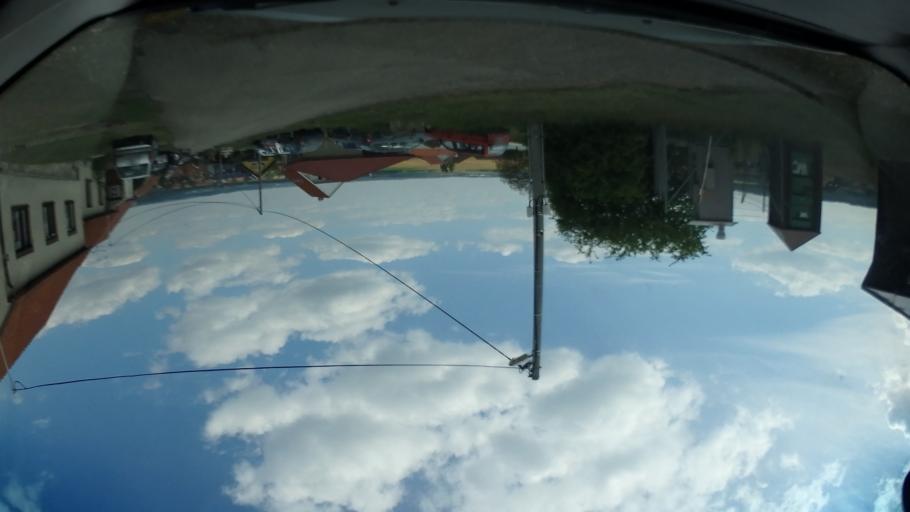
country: CZ
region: Vysocina
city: Mohelno
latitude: 49.1111
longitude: 16.1845
